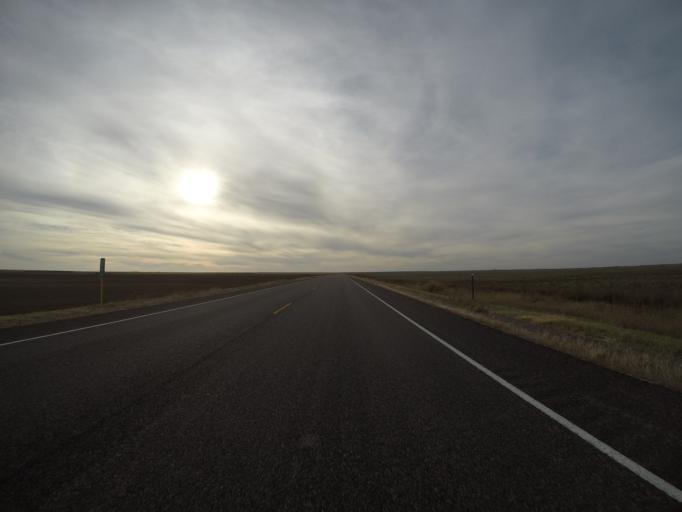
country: US
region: Kansas
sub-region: Cheyenne County
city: Saint Francis
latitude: 39.7464
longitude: -102.1005
